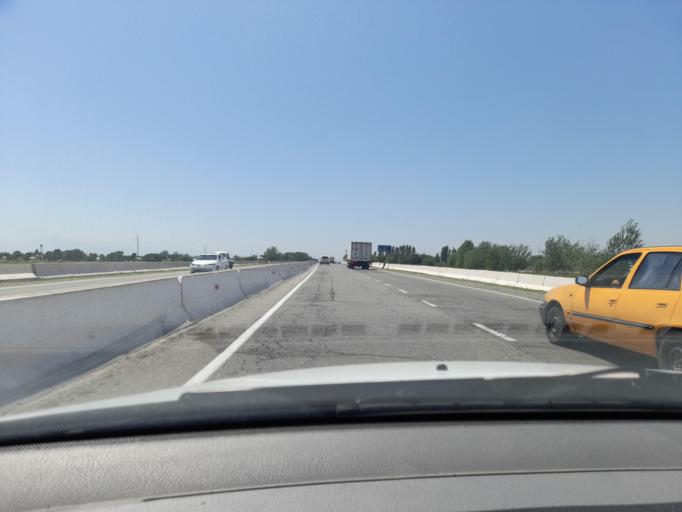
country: UZ
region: Jizzax
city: Paxtakor
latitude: 40.3209
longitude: 68.0959
